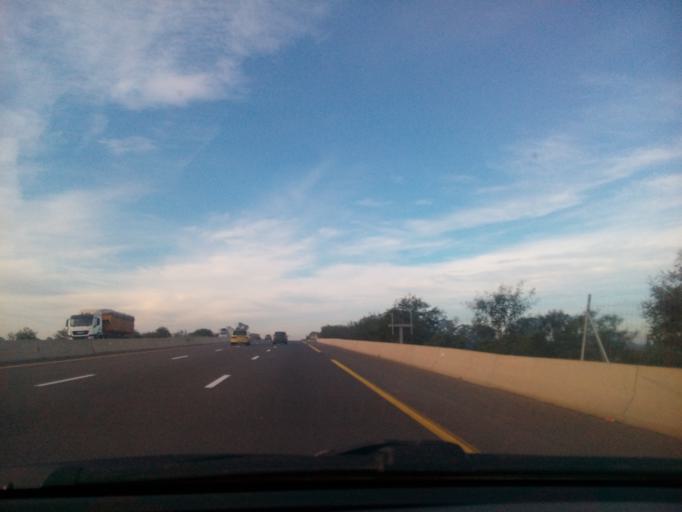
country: DZ
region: Mascara
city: Mascara
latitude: 35.6195
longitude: 0.0402
